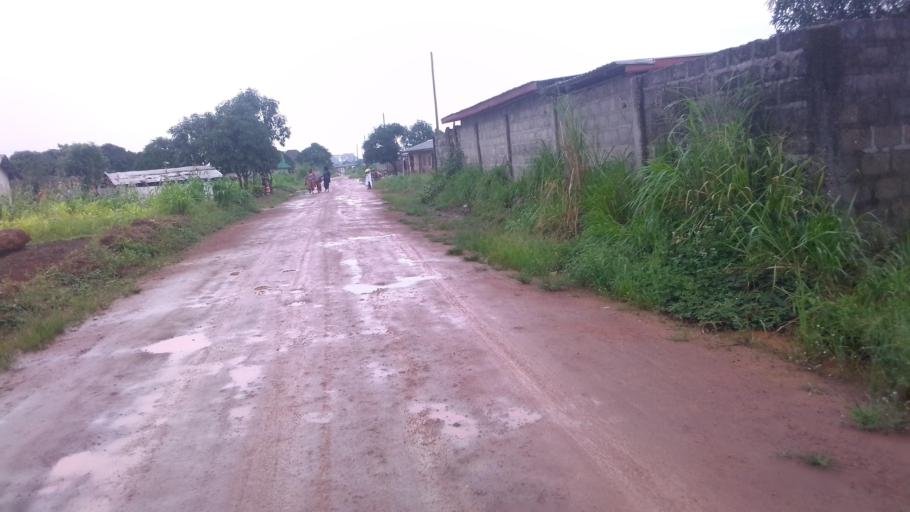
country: SL
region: Eastern Province
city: Hangha
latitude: 7.9123
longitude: -11.1648
